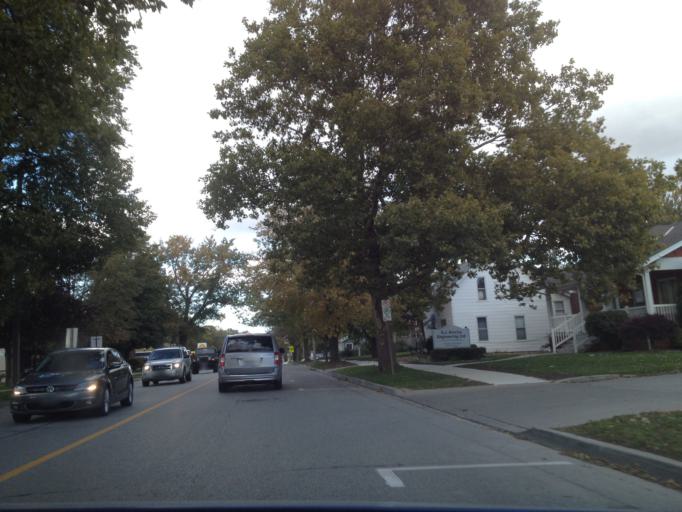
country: CA
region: Ontario
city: Amherstburg
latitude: 42.0390
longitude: -82.7395
